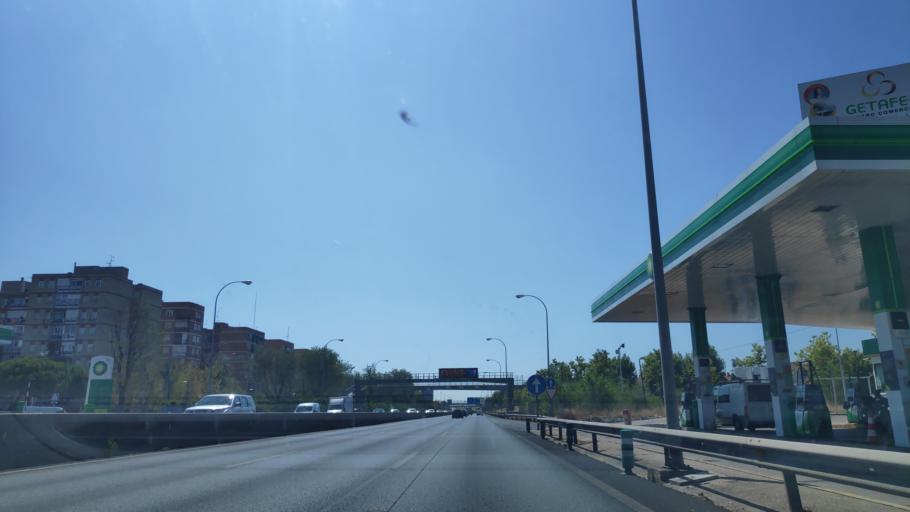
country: ES
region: Madrid
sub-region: Provincia de Madrid
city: Getafe
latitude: 40.3034
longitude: -3.7392
